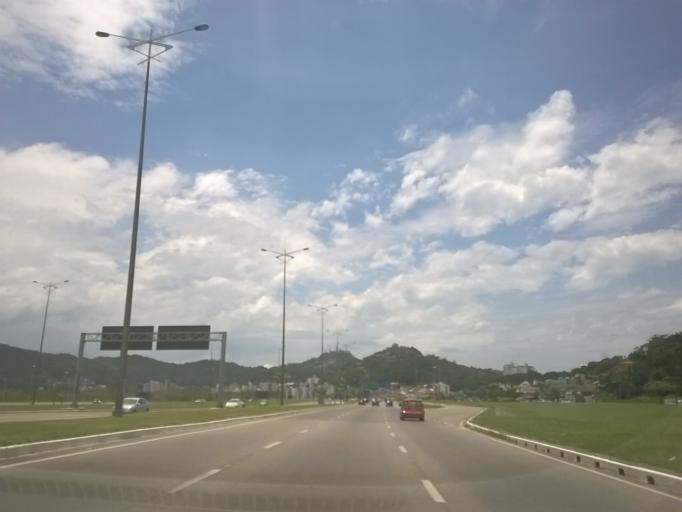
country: BR
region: Santa Catarina
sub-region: Florianopolis
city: Saco dos Limoes
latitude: -27.6213
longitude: -48.5279
